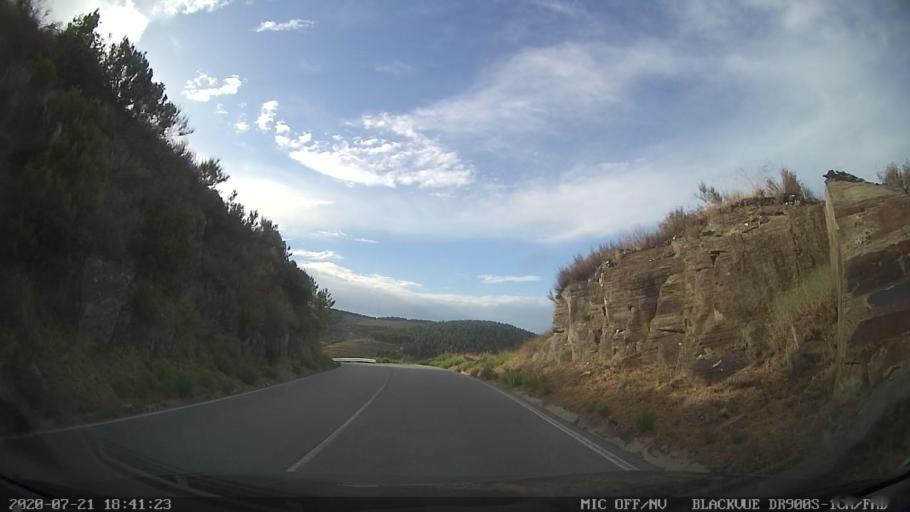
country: PT
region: Viseu
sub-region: Sao Joao da Pesqueira
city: Sao Joao da Pesqueira
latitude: 41.1064
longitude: -7.4625
